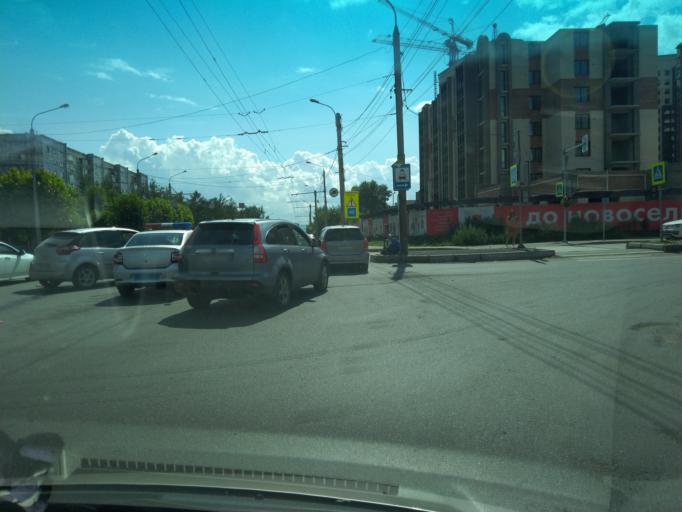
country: RU
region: Krasnoyarskiy
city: Solnechnyy
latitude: 56.0541
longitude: 92.9412
